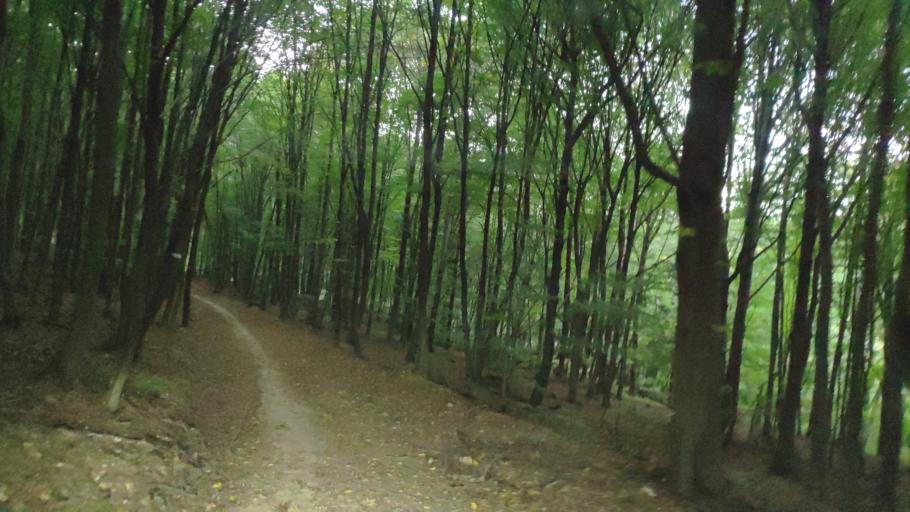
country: SK
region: Kosicky
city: Kosice
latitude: 48.7022
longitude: 21.1946
